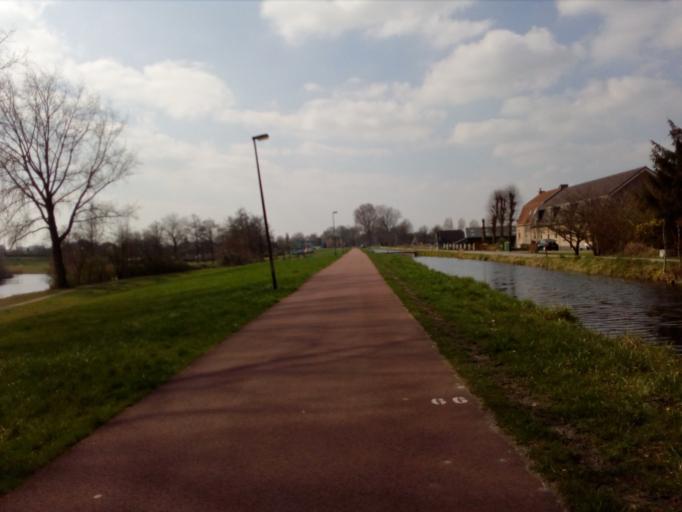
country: NL
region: South Holland
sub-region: Gemeente Zoetermeer
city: Zoetermeer
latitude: 52.0733
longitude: 4.4855
